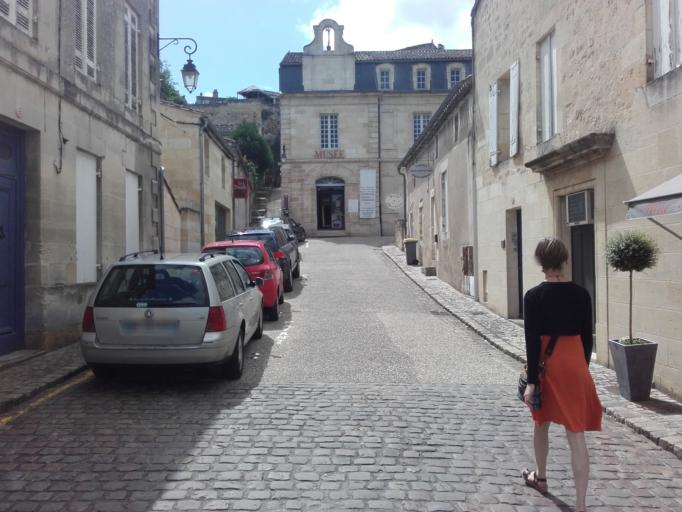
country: FR
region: Aquitaine
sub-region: Departement de la Gironde
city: Saint-Emilion
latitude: 44.8909
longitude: -0.1553
